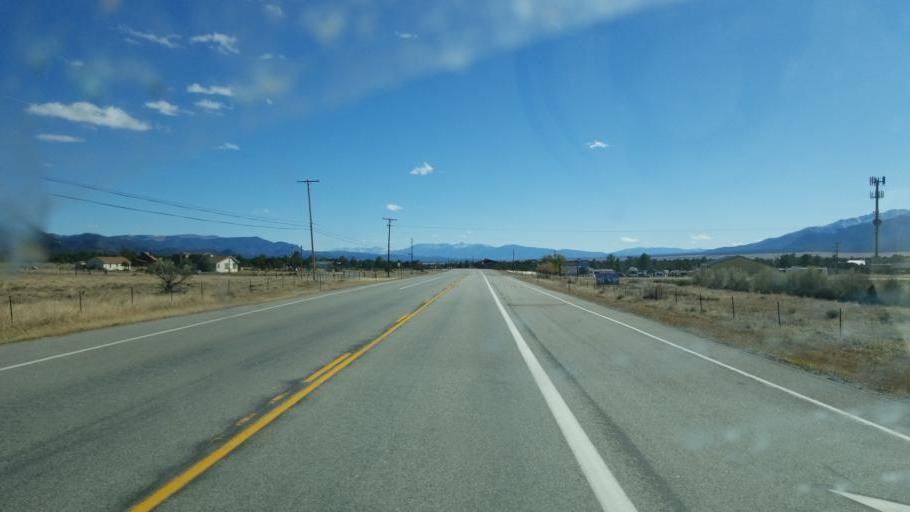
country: US
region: Colorado
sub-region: Chaffee County
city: Buena Vista
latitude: 38.8773
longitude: -106.1602
